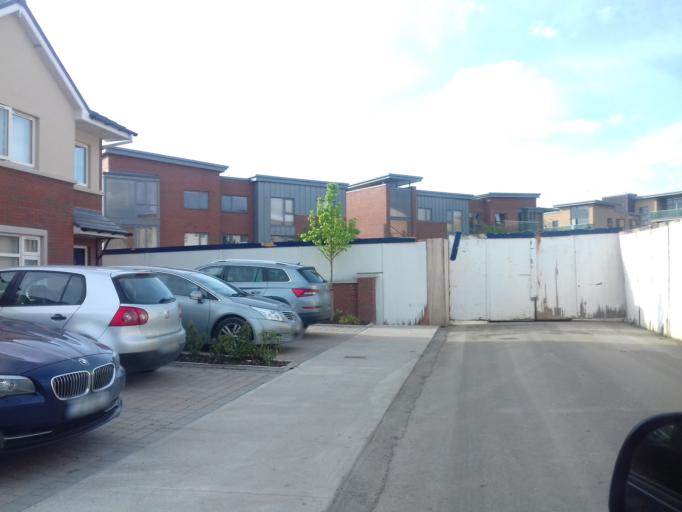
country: IE
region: Leinster
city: Chapelizod
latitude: 53.3717
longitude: -6.3397
